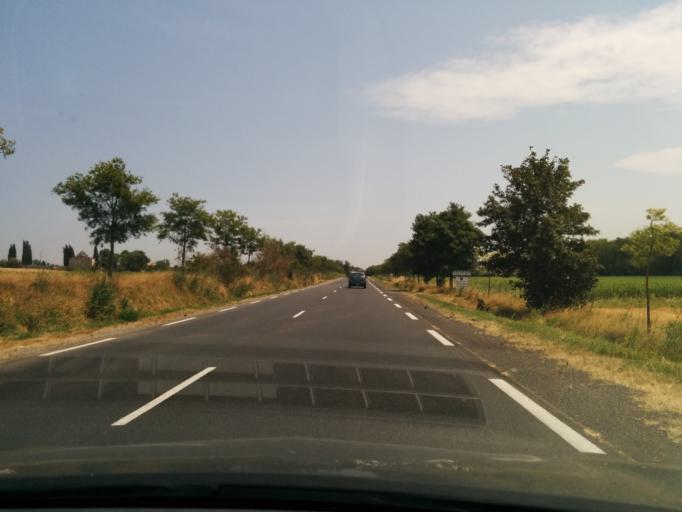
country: FR
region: Midi-Pyrenees
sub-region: Departement de la Haute-Garonne
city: Avignonet-Lauragais
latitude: 43.3599
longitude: 1.8124
